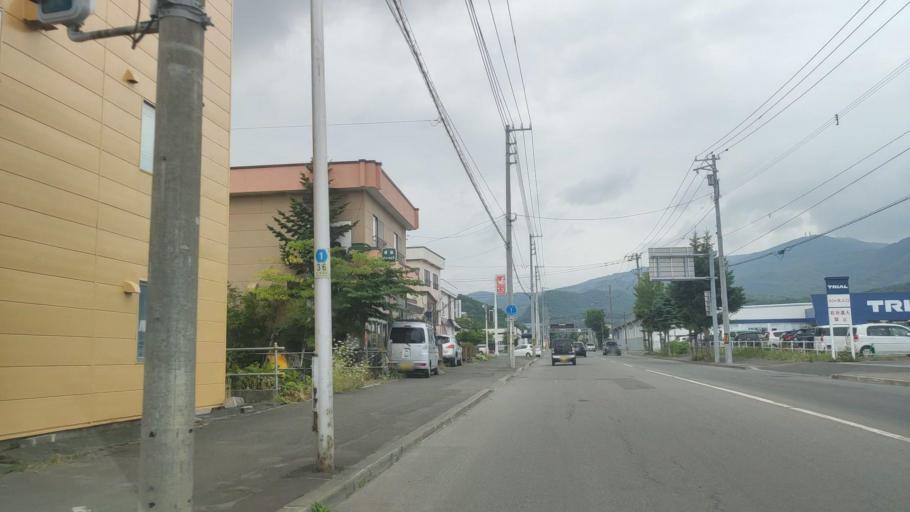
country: JP
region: Hokkaido
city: Otaru
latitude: 43.1661
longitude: 141.0501
